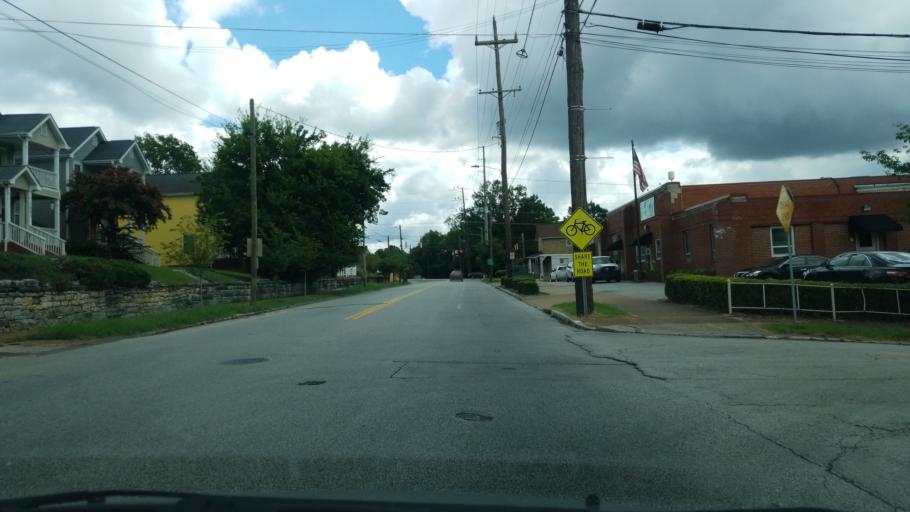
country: US
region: Tennessee
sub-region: Hamilton County
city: Chattanooga
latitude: 35.0383
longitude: -85.2947
